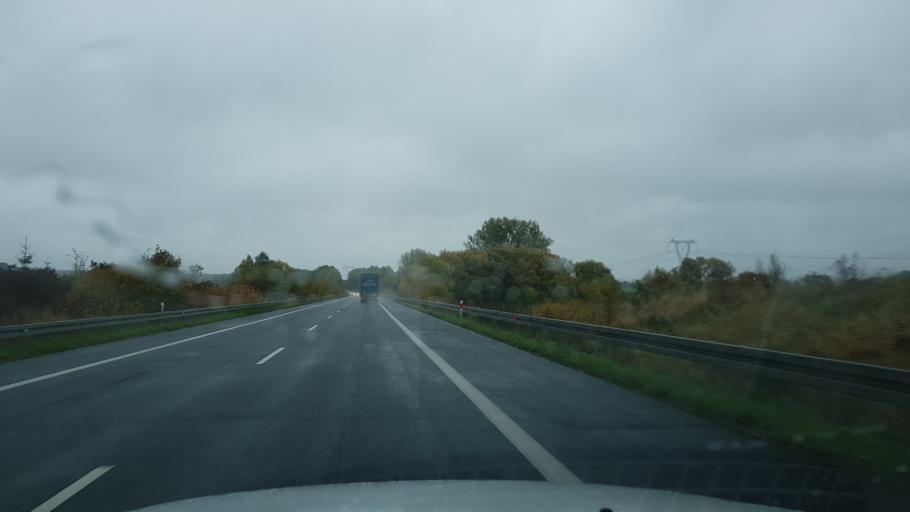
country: PL
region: West Pomeranian Voivodeship
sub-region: Powiat gryfinski
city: Stare Czarnowo
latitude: 53.2781
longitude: 14.7826
